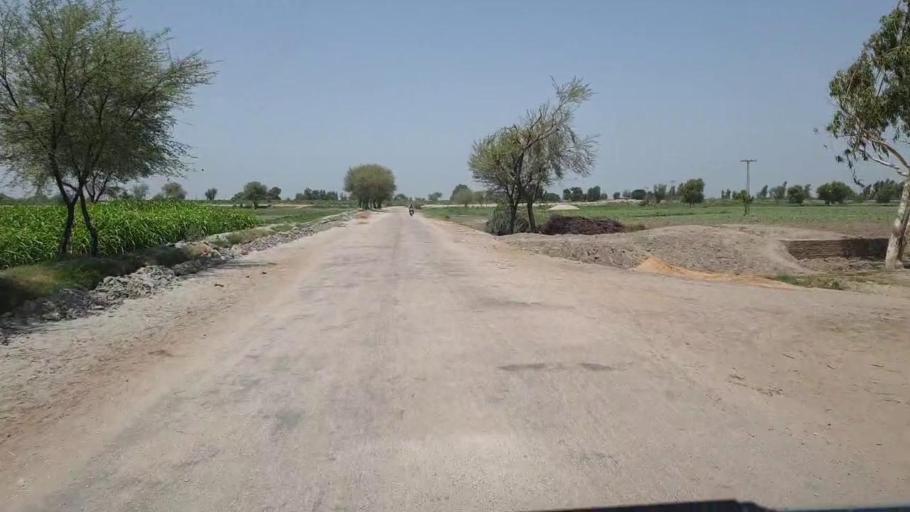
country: PK
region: Sindh
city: Nawabshah
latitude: 26.3451
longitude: 68.3871
